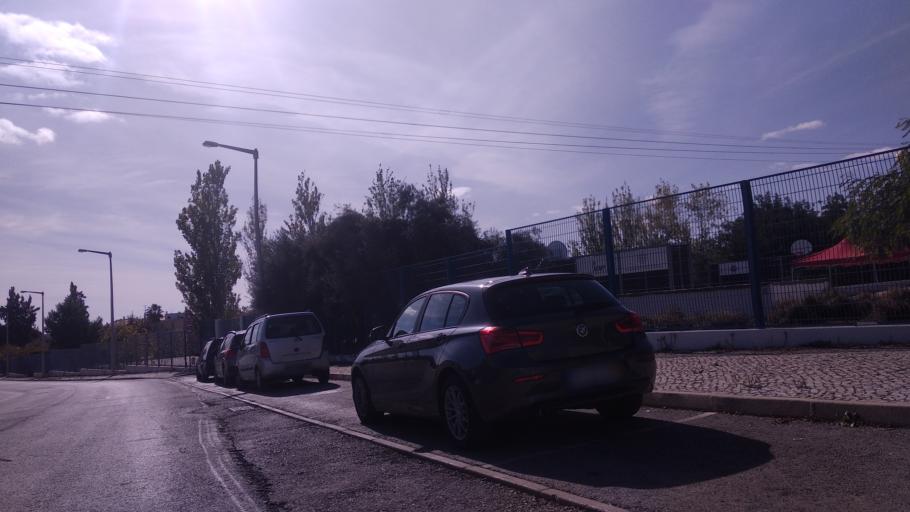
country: PT
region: Faro
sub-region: Sao Bras de Alportel
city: Sao Bras de Alportel
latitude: 37.1589
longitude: -7.8854
